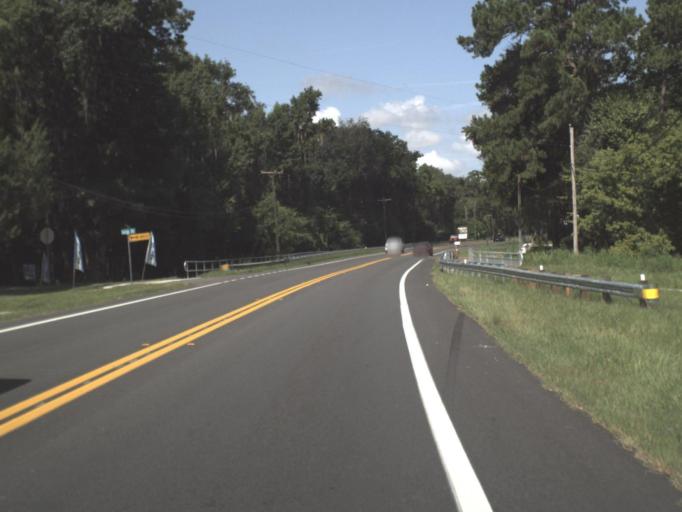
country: US
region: Florida
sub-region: Hernando County
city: Brooksville
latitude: 28.5530
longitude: -82.4076
